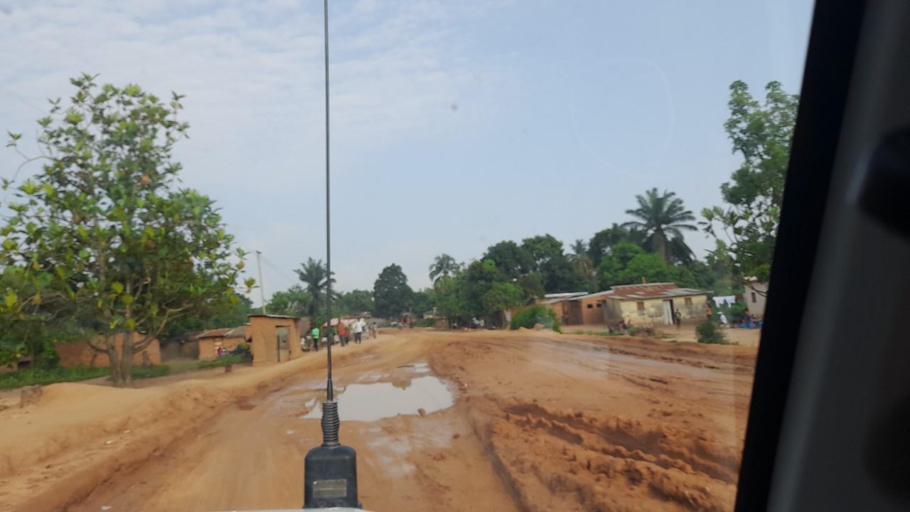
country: CD
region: Kasai-Occidental
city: Kananga
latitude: -5.8909
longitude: 22.3745
